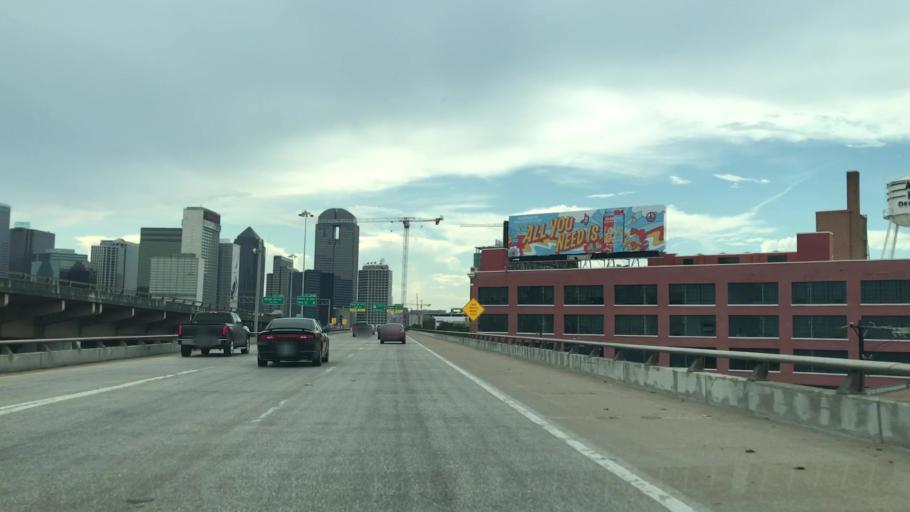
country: US
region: Texas
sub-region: Dallas County
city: Dallas
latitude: 32.7808
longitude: -96.7832
